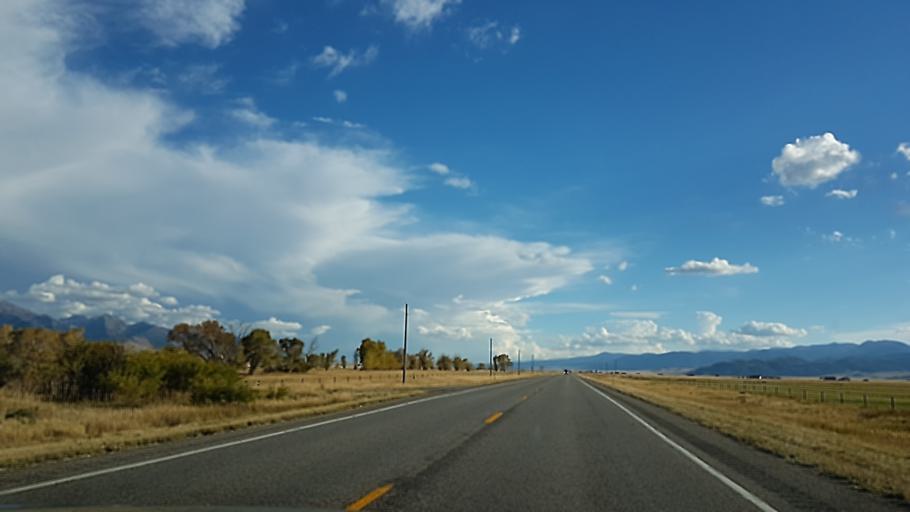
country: US
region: Montana
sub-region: Madison County
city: Virginia City
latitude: 45.1995
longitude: -111.6788
